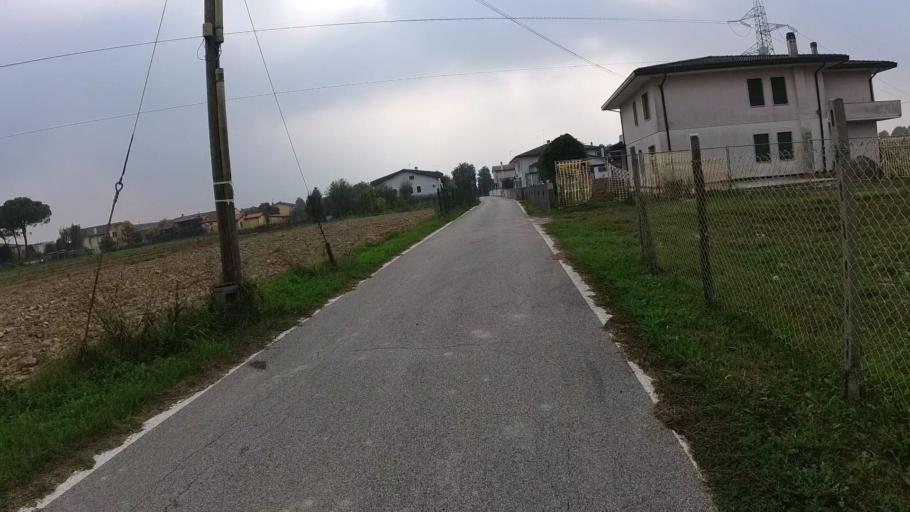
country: IT
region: Veneto
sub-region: Provincia di Venezia
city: Fosso
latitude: 45.3890
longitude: 12.0383
